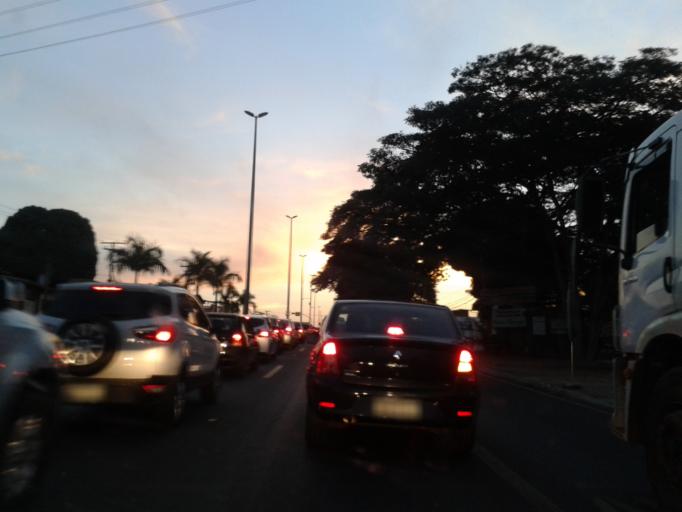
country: BR
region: Goias
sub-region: Goiania
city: Goiania
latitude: -16.6600
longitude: -49.3361
